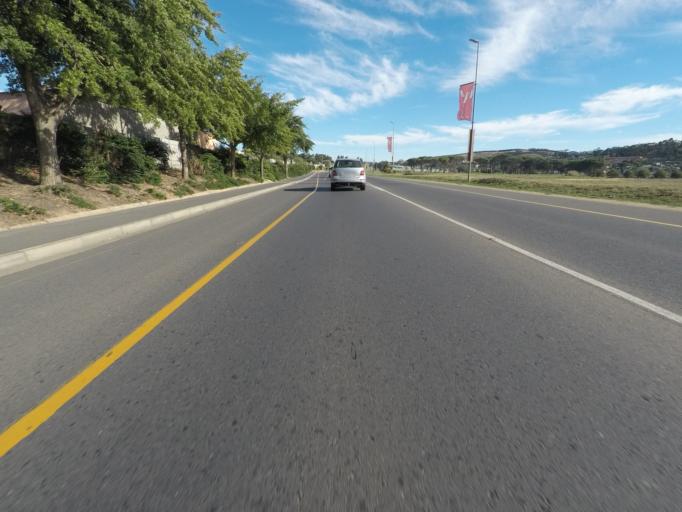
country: ZA
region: Western Cape
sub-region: Cape Winelands District Municipality
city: Stellenbosch
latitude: -33.9150
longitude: 18.8497
